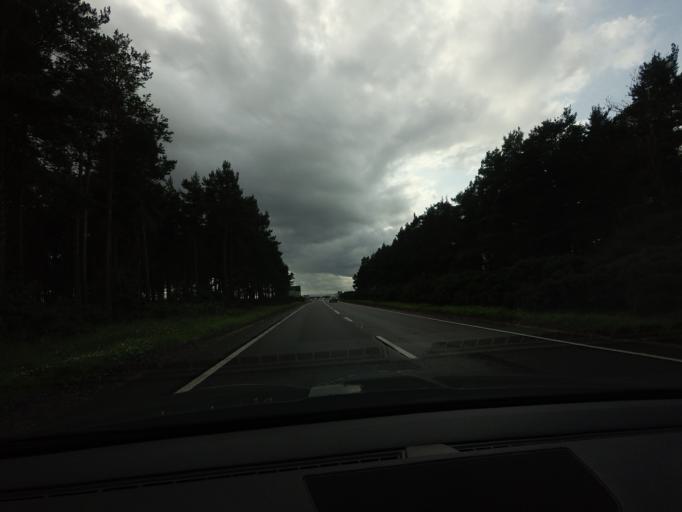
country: GB
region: Scotland
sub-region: Highland
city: Nairn
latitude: 57.5471
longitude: -3.9973
